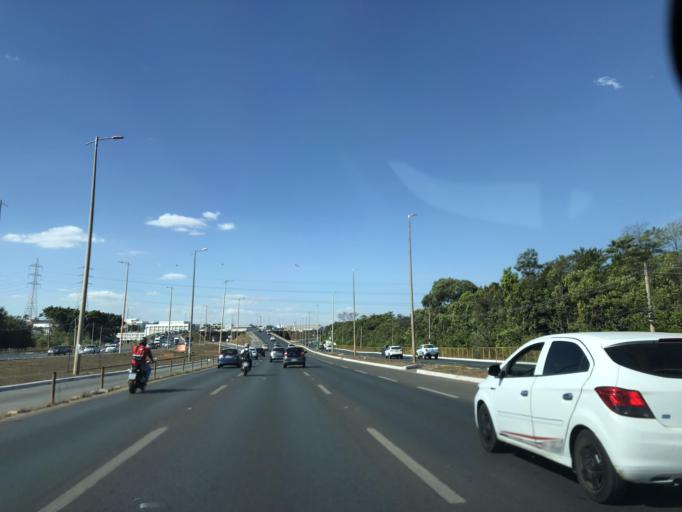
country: BR
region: Federal District
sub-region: Brasilia
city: Brasilia
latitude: -15.8103
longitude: -47.9708
